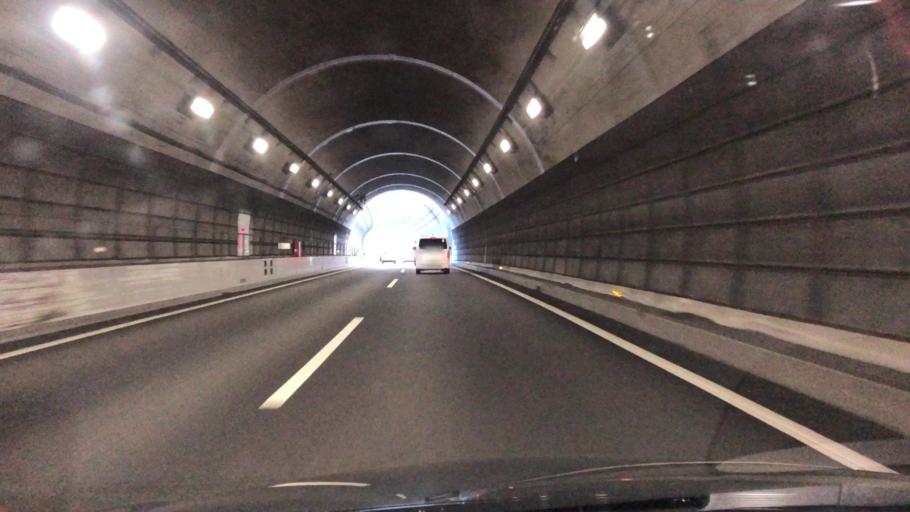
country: JP
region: Tokyo
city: Itsukaichi
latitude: 35.6885
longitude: 139.2600
